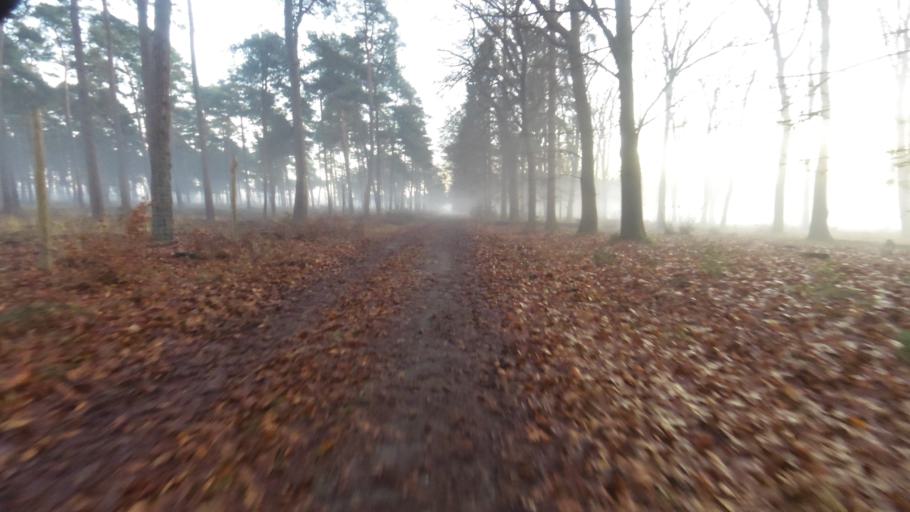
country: NL
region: Gelderland
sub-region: Gemeente Apeldoorn
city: Uddel
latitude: 52.2360
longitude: 5.7871
